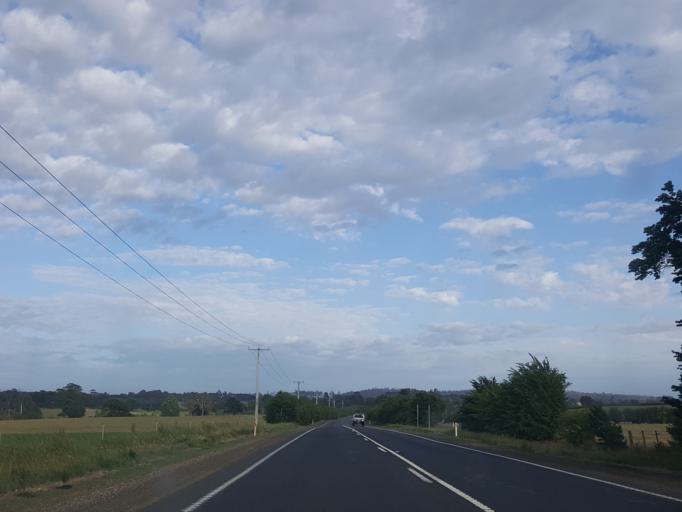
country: AU
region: Tasmania
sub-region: Northern Midlands
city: Perth
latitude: -41.5907
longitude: 147.1956
